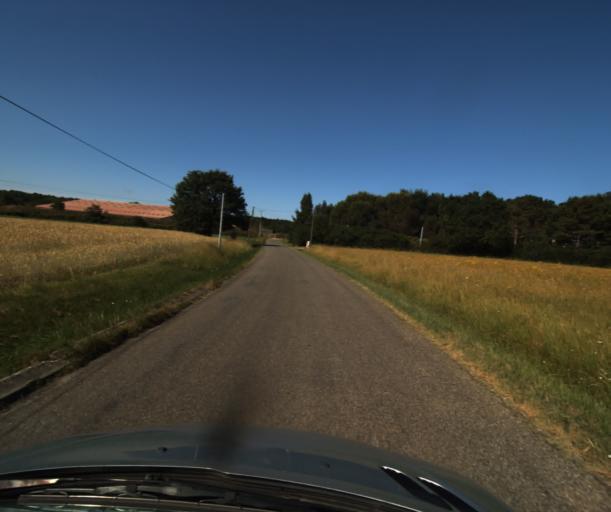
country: FR
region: Midi-Pyrenees
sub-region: Departement du Tarn-et-Garonne
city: Campsas
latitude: 43.9237
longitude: 1.2904
